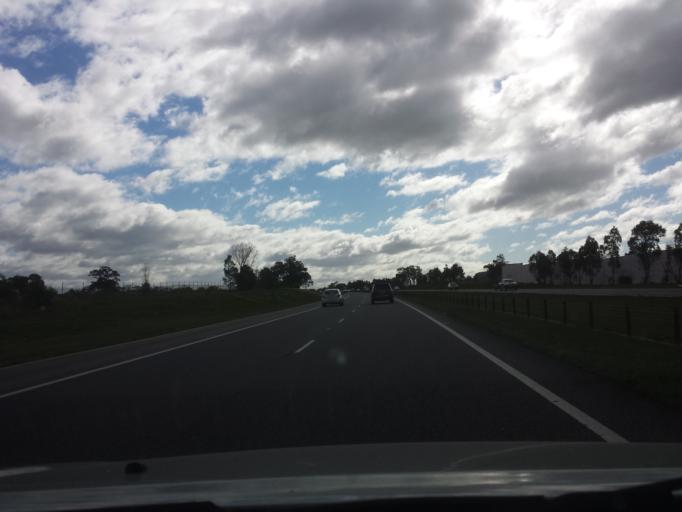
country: AU
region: Victoria
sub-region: Hume
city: Craigieburn
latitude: -37.6216
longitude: 144.9921
